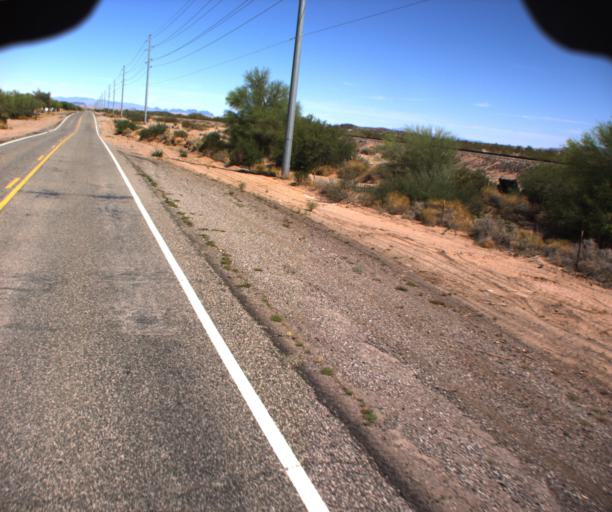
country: US
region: Arizona
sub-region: La Paz County
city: Cienega Springs
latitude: 33.9495
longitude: -114.0199
